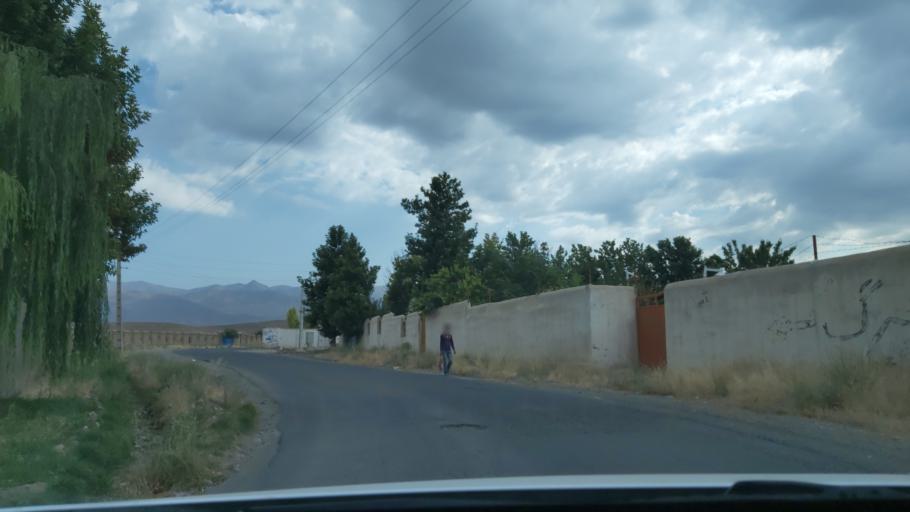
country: IR
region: Alborz
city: Hashtgerd
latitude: 35.9519
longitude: 50.7756
